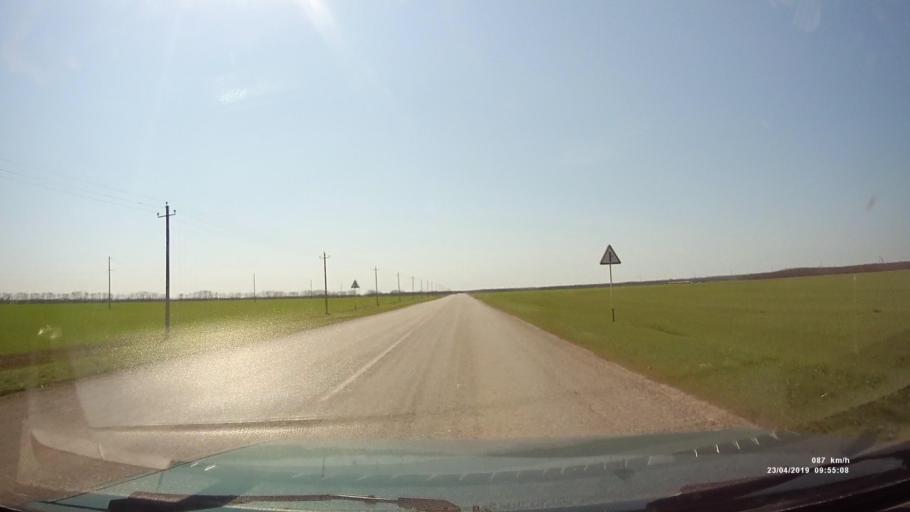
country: RU
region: Rostov
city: Orlovskiy
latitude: 46.8124
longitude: 42.0605
